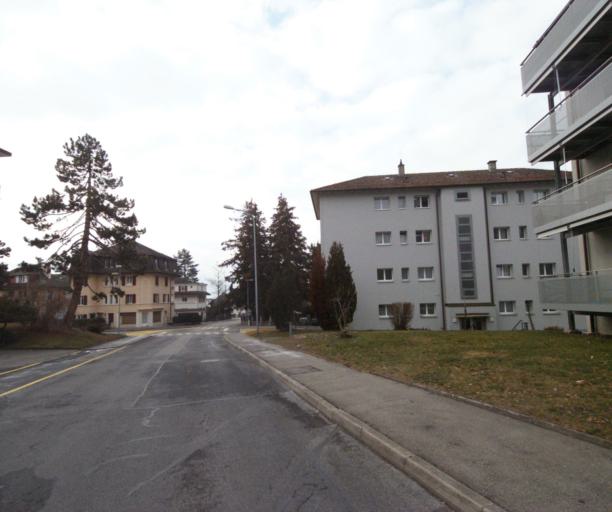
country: CH
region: Vaud
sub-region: Riviera-Pays-d'Enhaut District
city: La Tour-de-Peilz
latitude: 46.4550
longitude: 6.8630
